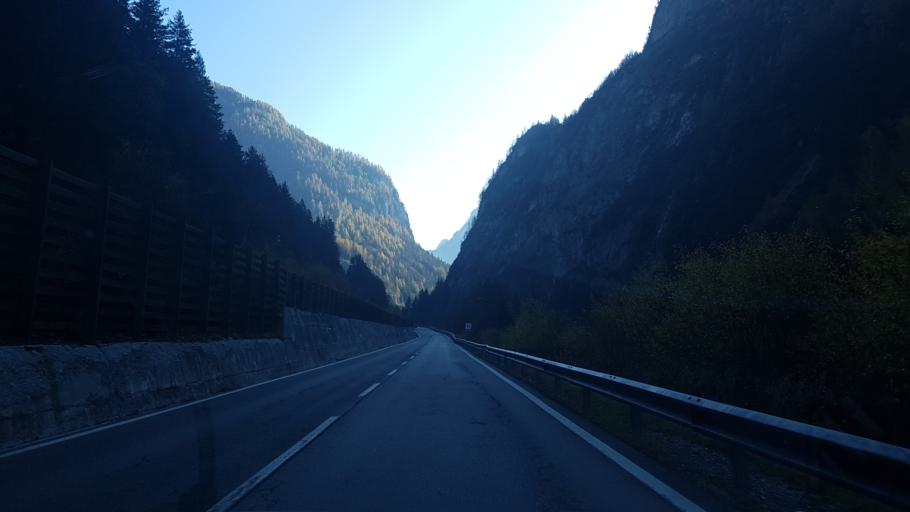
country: IT
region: Veneto
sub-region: Provincia di Belluno
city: San Pietro di Cadore
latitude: 46.5805
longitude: 12.6309
